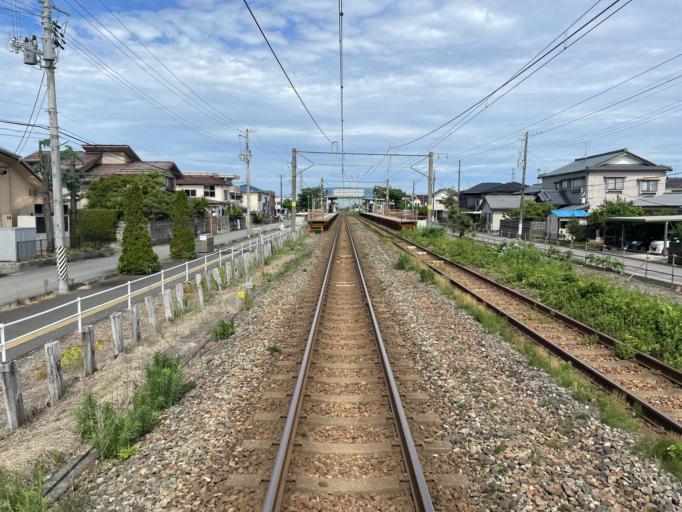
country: JP
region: Niigata
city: Kameda-honcho
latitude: 37.9208
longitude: 139.1799
